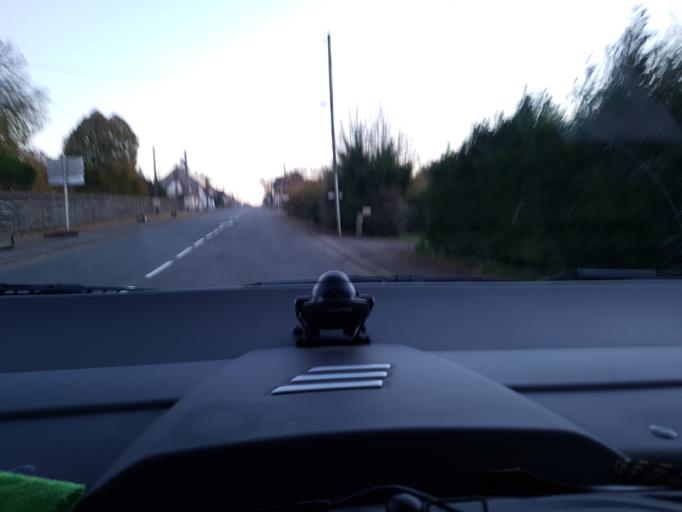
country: FR
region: Picardie
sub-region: Departement de la Somme
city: Rue
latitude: 50.3148
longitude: 1.7503
